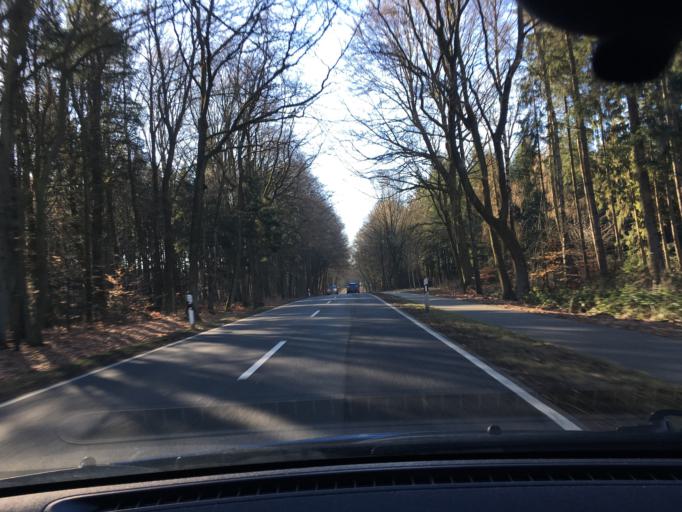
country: DE
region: Lower Saxony
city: Hanstedt Eins
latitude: 53.0785
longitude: 10.4052
